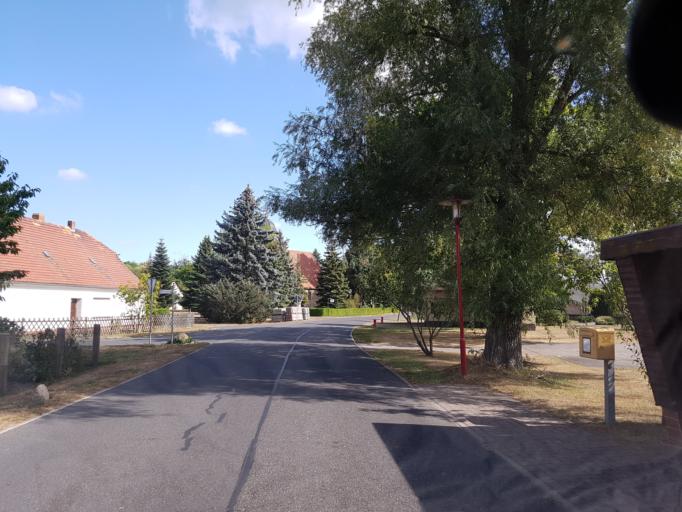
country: DE
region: Brandenburg
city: Sonnewalde
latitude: 51.7330
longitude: 13.6277
